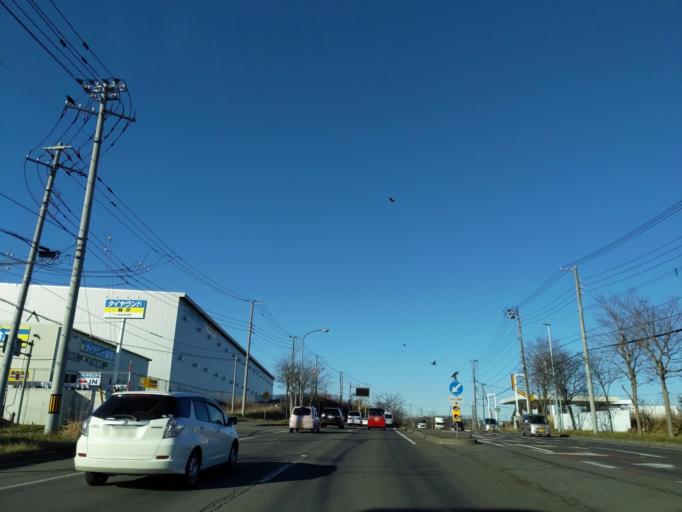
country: JP
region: Hokkaido
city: Kitahiroshima
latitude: 42.9510
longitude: 141.4973
